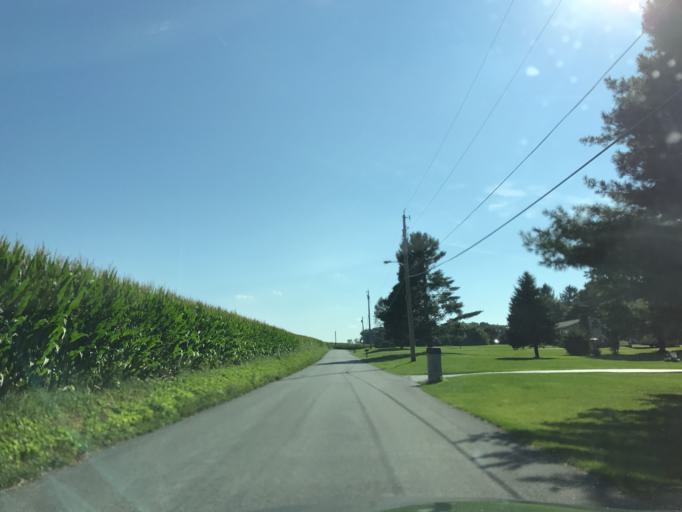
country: US
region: Pennsylvania
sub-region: York County
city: Stewartstown
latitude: 39.6622
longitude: -76.5673
